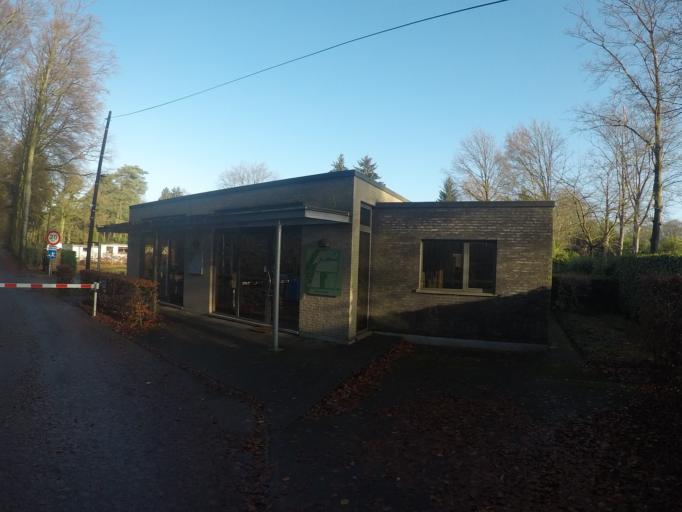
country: BE
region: Flanders
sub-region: Provincie Antwerpen
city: Brasschaat
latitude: 51.2908
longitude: 4.5344
